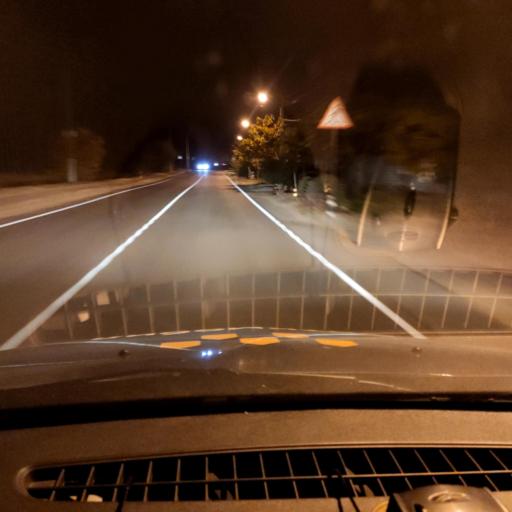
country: RU
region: Voronezj
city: Shilovo
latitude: 51.6013
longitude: 39.0341
